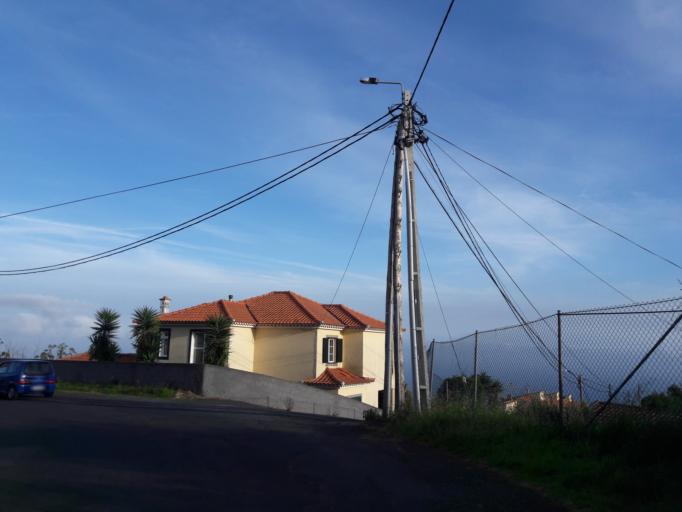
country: PT
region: Madeira
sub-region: Santa Cruz
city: Camacha
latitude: 32.6662
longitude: -16.8424
